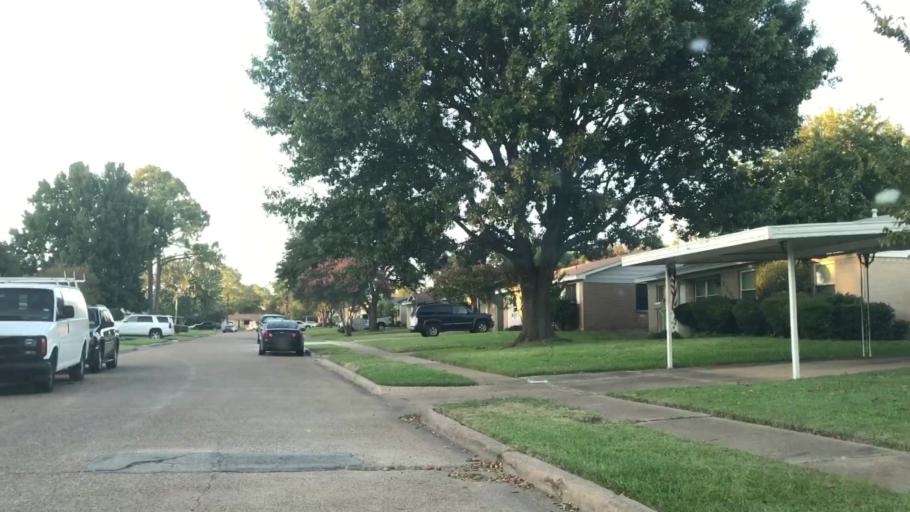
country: US
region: Texas
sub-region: Dallas County
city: Mesquite
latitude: 32.7505
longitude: -96.5808
